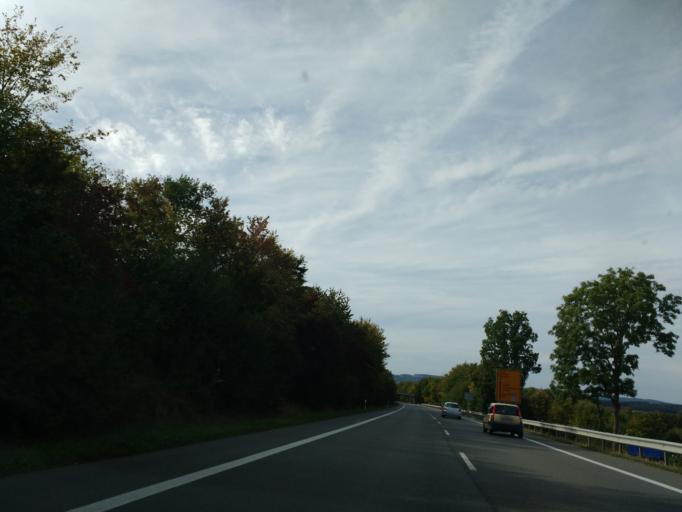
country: DE
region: North Rhine-Westphalia
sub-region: Regierungsbezirk Detmold
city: Nieheim
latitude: 51.8070
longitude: 9.1236
